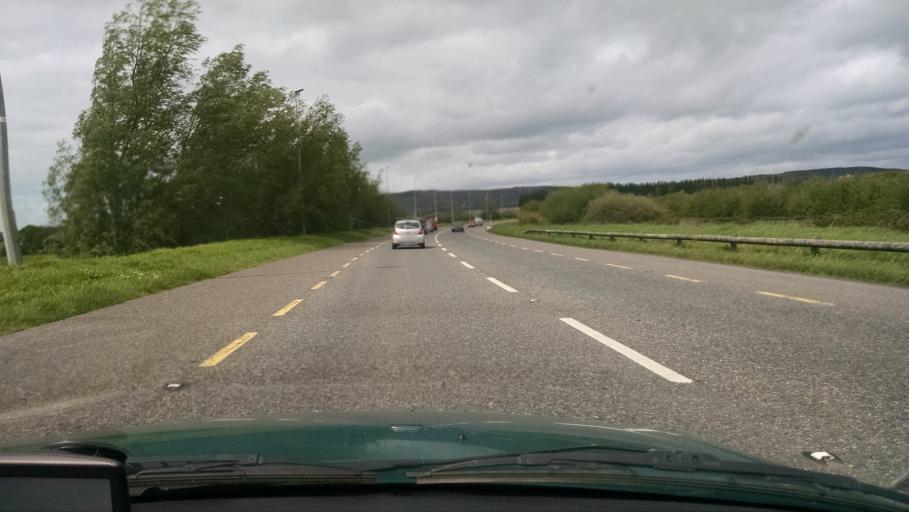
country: IE
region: Munster
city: Moyross
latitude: 52.6686
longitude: -8.6739
